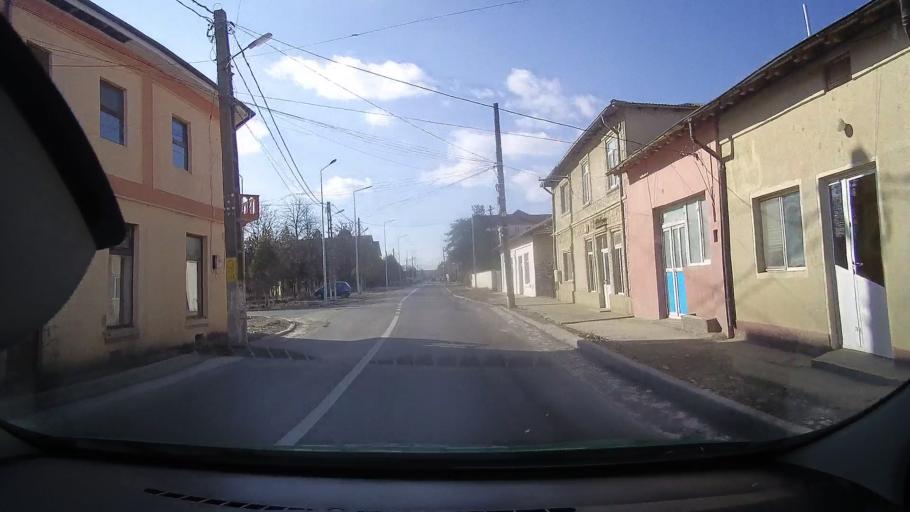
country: RO
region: Constanta
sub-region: Comuna Cogealac
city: Cogealac
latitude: 44.5575
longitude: 28.5661
